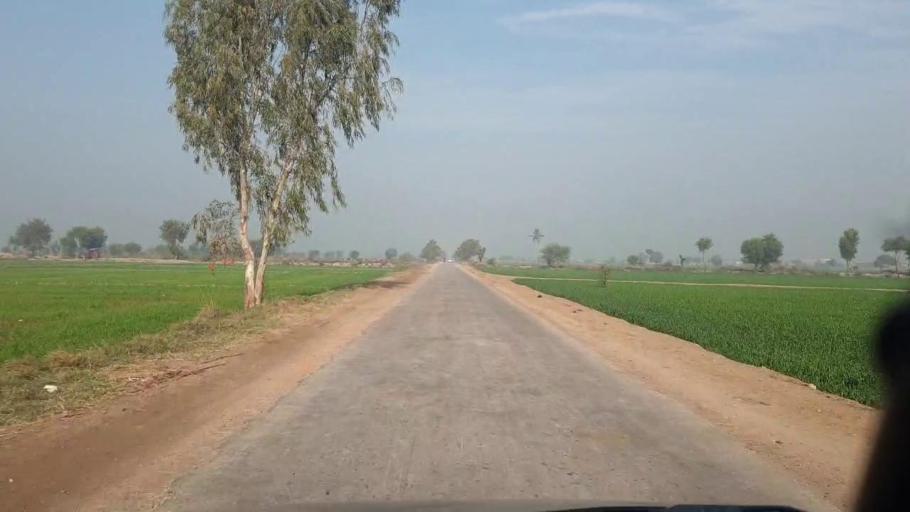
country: PK
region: Sindh
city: Shahdadpur
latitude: 25.9665
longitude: 68.5820
